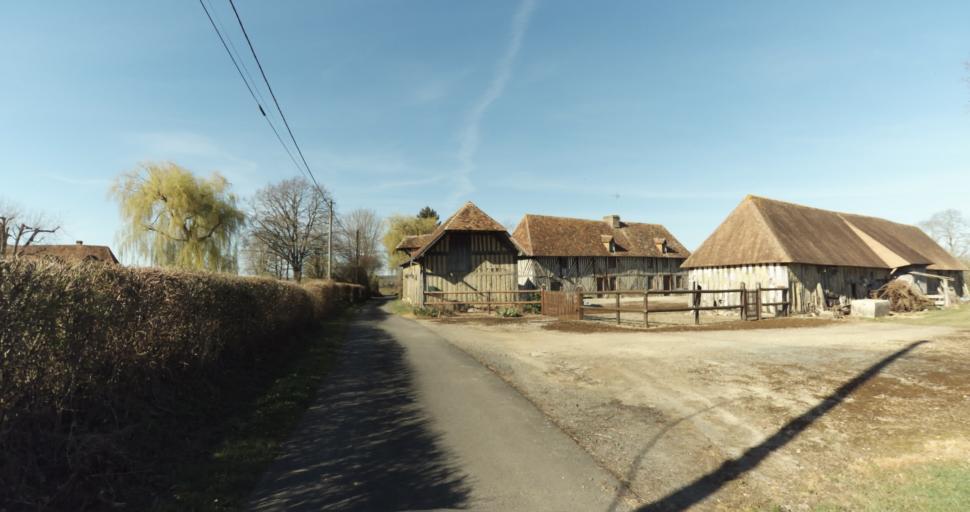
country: FR
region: Lower Normandy
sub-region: Departement du Calvados
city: Saint-Pierre-sur-Dives
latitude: 49.0389
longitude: 0.0578
